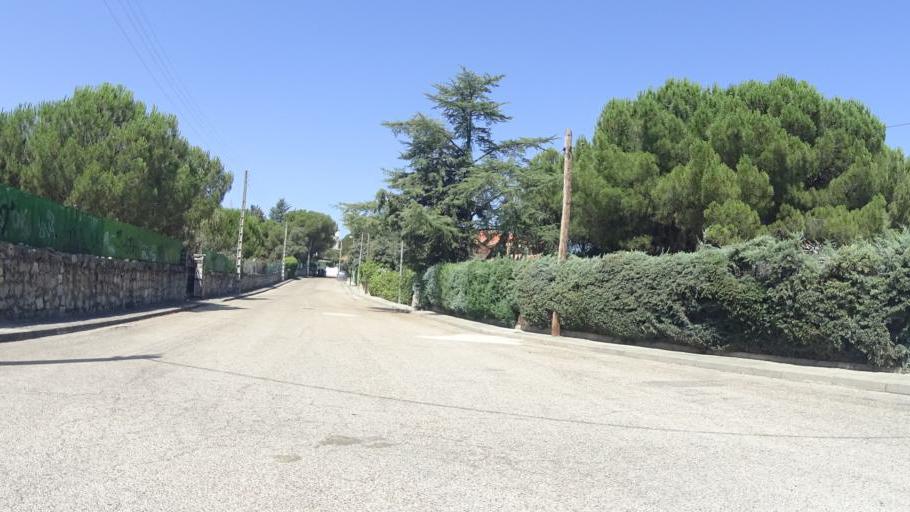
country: ES
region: Madrid
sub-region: Provincia de Madrid
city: Colmenarejo
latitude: 40.5585
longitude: -4.0068
